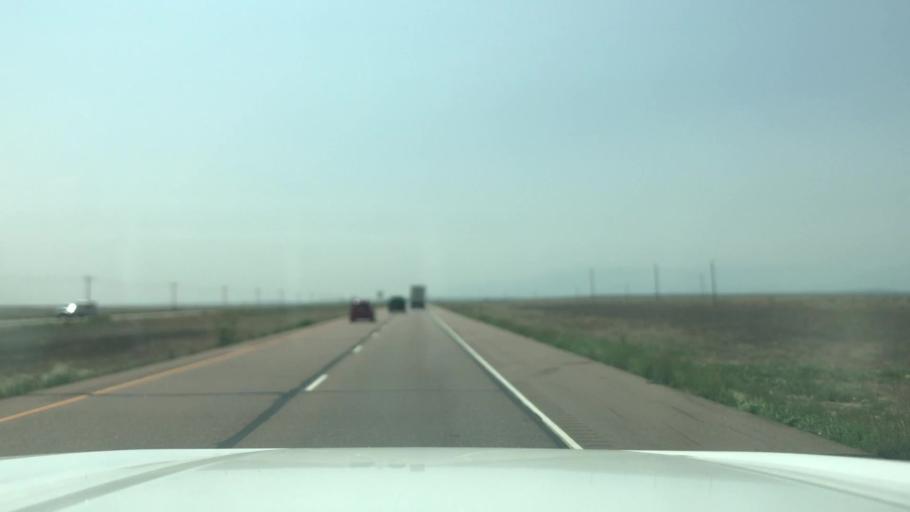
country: US
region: Colorado
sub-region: Pueblo County
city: Pueblo
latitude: 38.1556
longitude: -104.6487
